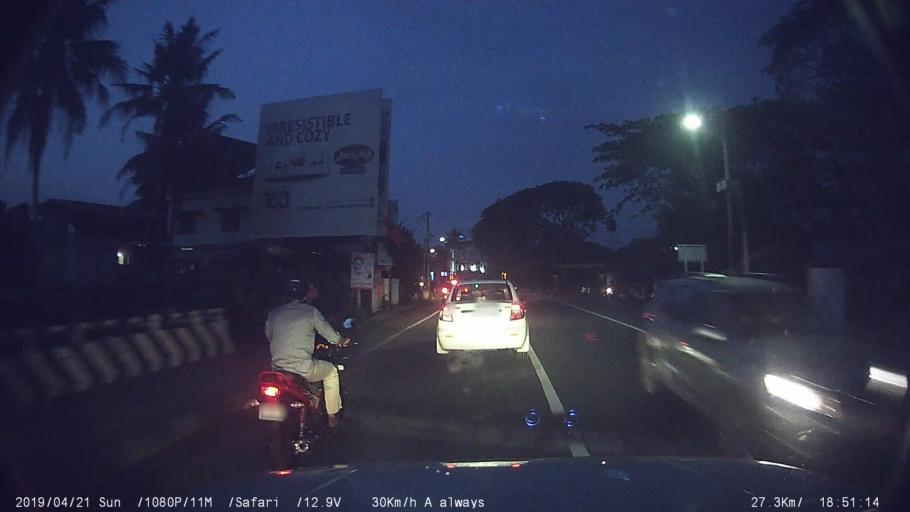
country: IN
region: Kerala
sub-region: Kottayam
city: Kottayam
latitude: 9.6219
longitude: 76.5358
